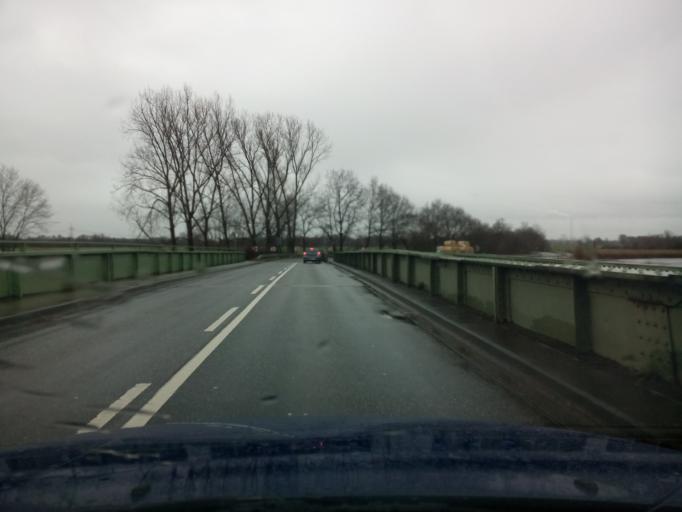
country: DE
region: Lower Saxony
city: Ritterhude
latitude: 53.1769
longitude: 8.7499
